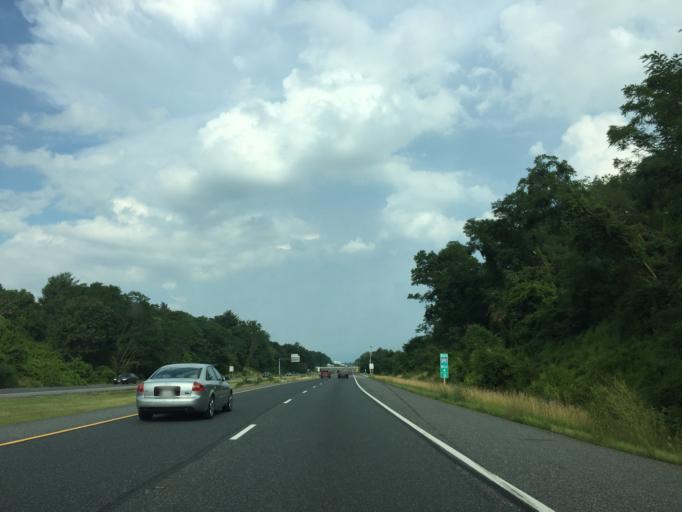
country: US
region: Maryland
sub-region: Baltimore County
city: Lansdowne
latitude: 39.2337
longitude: -76.6588
